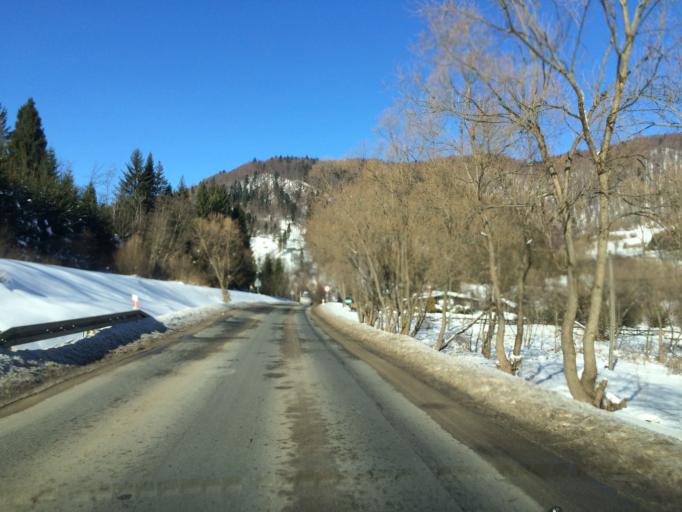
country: PL
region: Subcarpathian Voivodeship
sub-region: Powiat leski
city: Cisna
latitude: 49.2227
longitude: 22.3615
